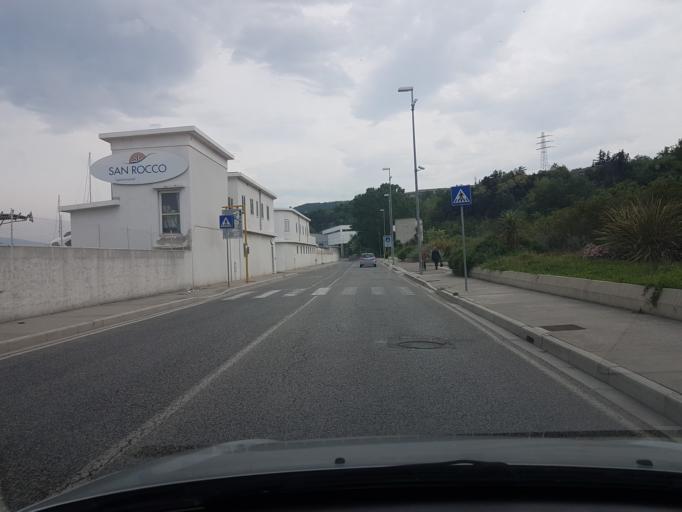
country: IT
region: Friuli Venezia Giulia
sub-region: Provincia di Trieste
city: Muggia
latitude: 45.6024
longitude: 13.7755
